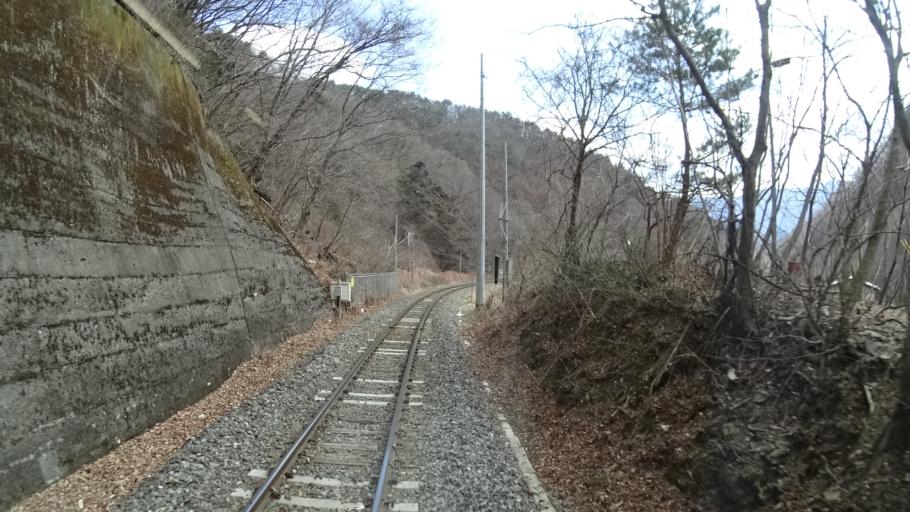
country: JP
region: Iwate
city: Kamaishi
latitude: 39.2753
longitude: 141.7235
